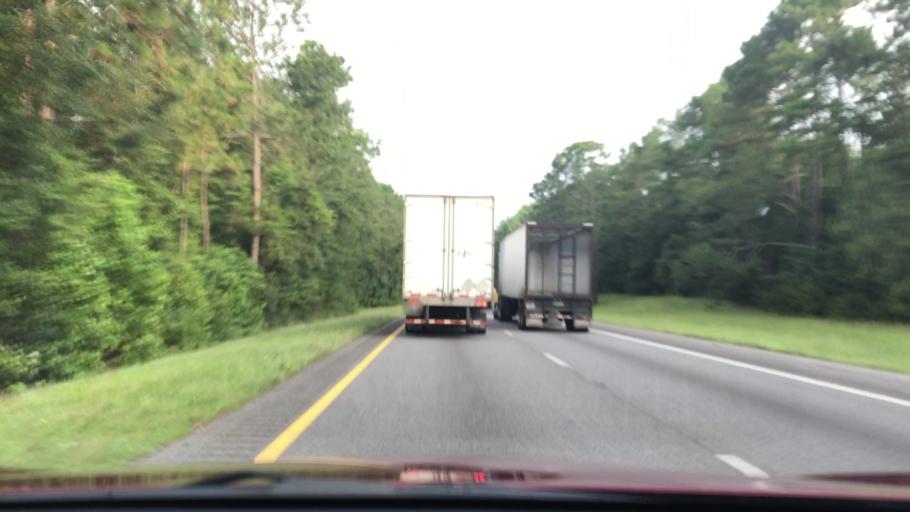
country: US
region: South Carolina
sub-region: Dorchester County
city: Ridgeville
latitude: 33.1554
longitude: -80.3471
